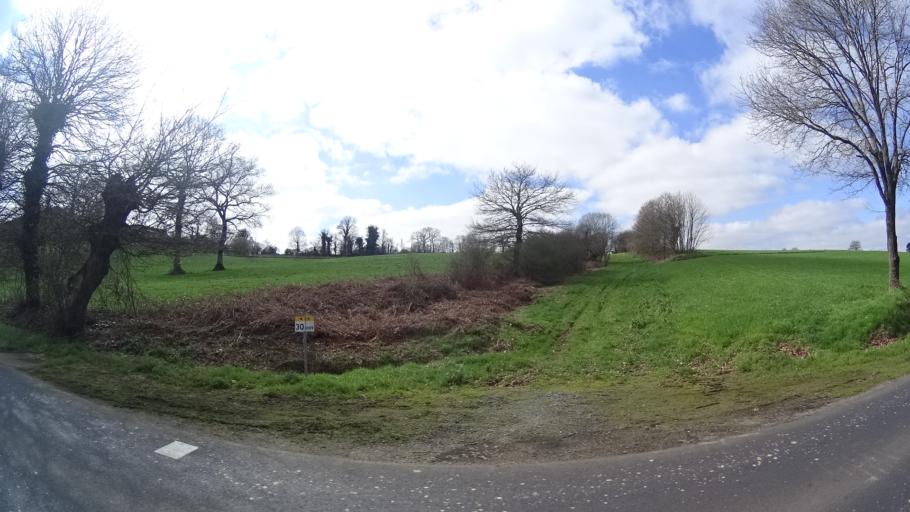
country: FR
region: Brittany
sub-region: Departement du Morbihan
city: Caro
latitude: 47.8411
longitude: -2.3157
